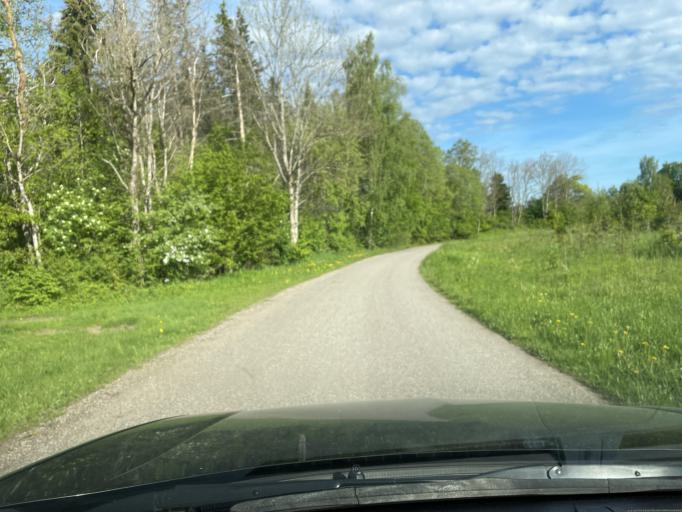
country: EE
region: Harju
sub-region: Keila linn
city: Keila
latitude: 59.3084
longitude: 24.2824
